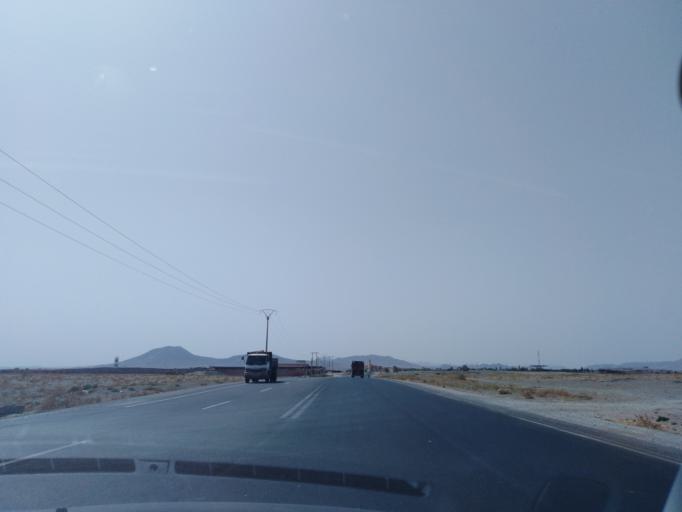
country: MA
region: Marrakech-Tensift-Al Haouz
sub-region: Marrakech
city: Marrakesh
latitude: 31.7690
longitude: -8.1246
